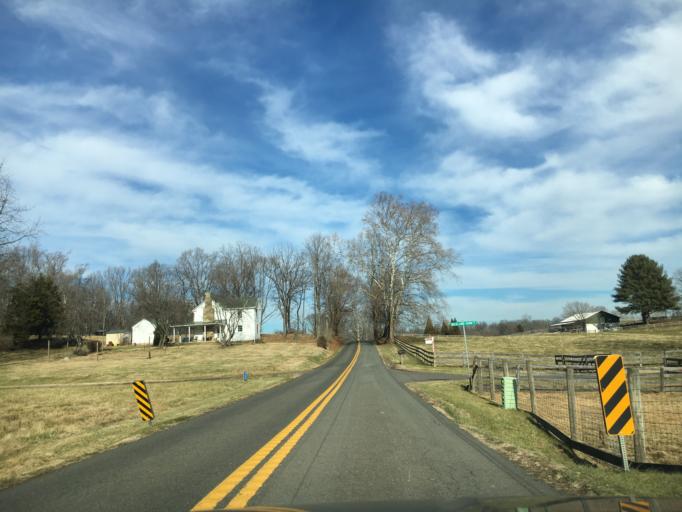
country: US
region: Virginia
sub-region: Warren County
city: Apple Mountain Lake
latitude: 38.8198
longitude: -78.0013
